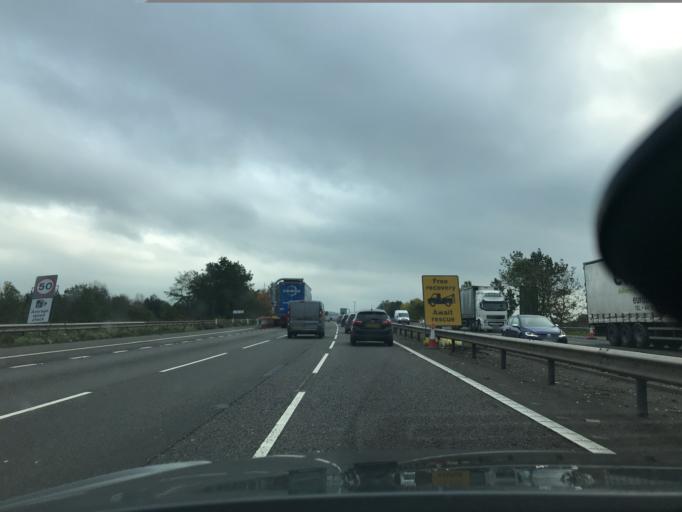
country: GB
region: England
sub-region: Staffordshire
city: Stafford
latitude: 52.7657
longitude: -2.1103
